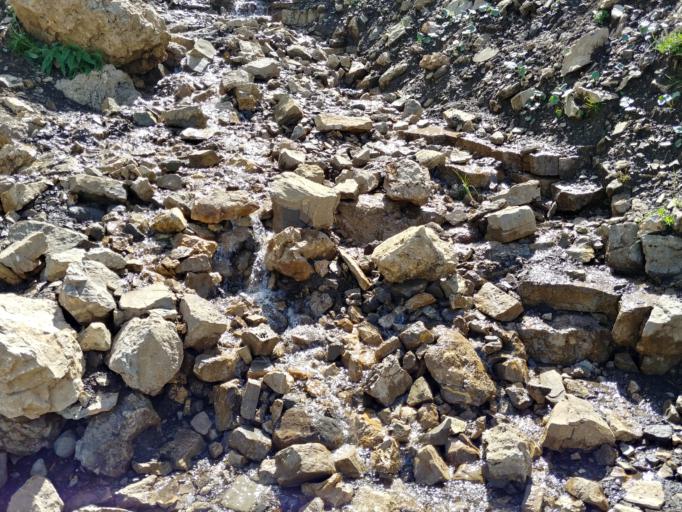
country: IT
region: Trentino-Alto Adige
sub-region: Provincia di Trento
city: Mazzin
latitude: 46.5096
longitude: 11.7002
